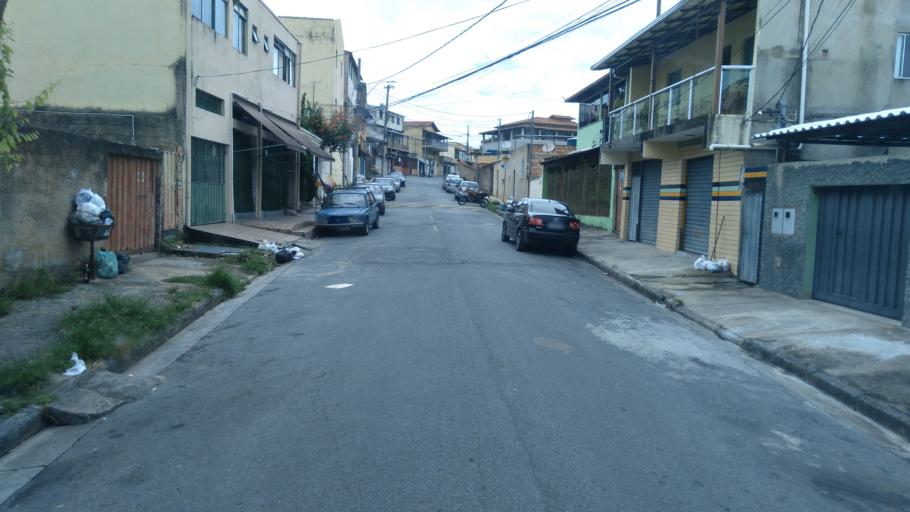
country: BR
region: Minas Gerais
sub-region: Belo Horizonte
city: Belo Horizonte
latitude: -19.8467
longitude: -43.9059
